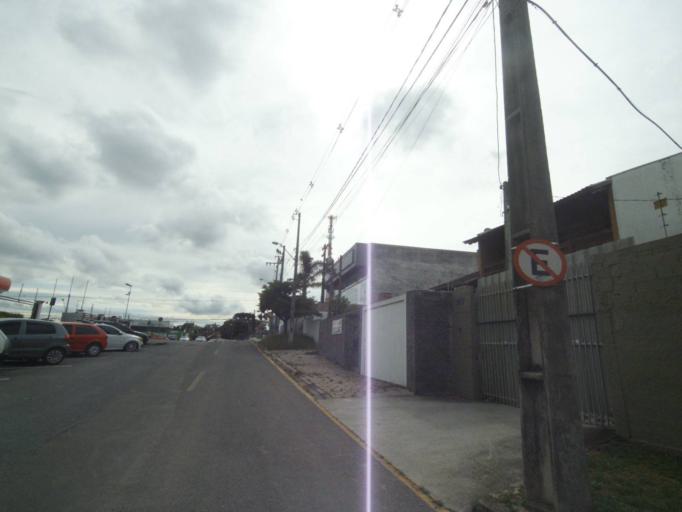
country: BR
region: Parana
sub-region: Curitiba
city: Curitiba
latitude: -25.4414
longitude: -49.3052
